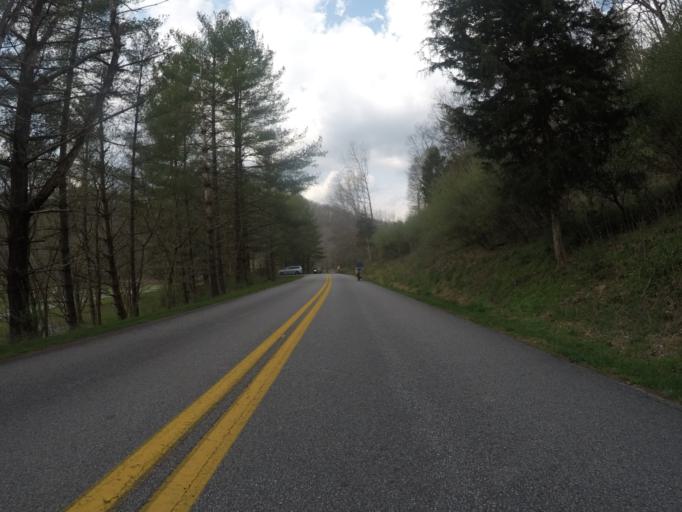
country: US
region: West Virginia
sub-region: Wayne County
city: Lavalette
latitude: 38.3085
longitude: -82.3563
